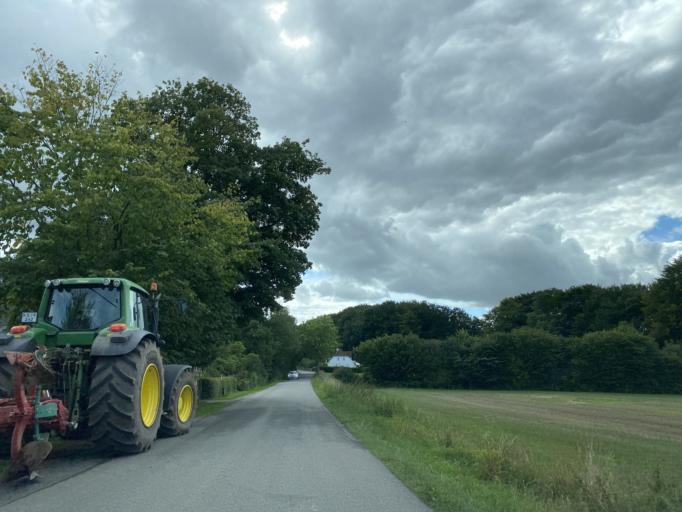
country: DK
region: Central Jutland
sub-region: Horsens Kommune
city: Horsens
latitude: 55.9569
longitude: 9.8567
